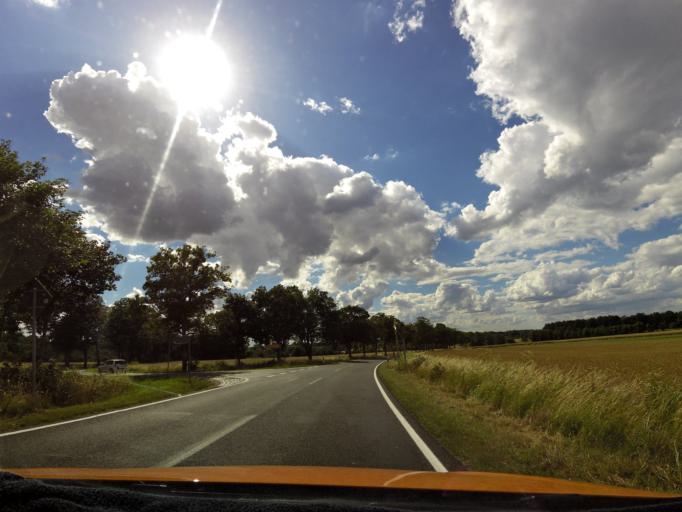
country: DE
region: Brandenburg
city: Rangsdorf
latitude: 52.3084
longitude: 13.4873
